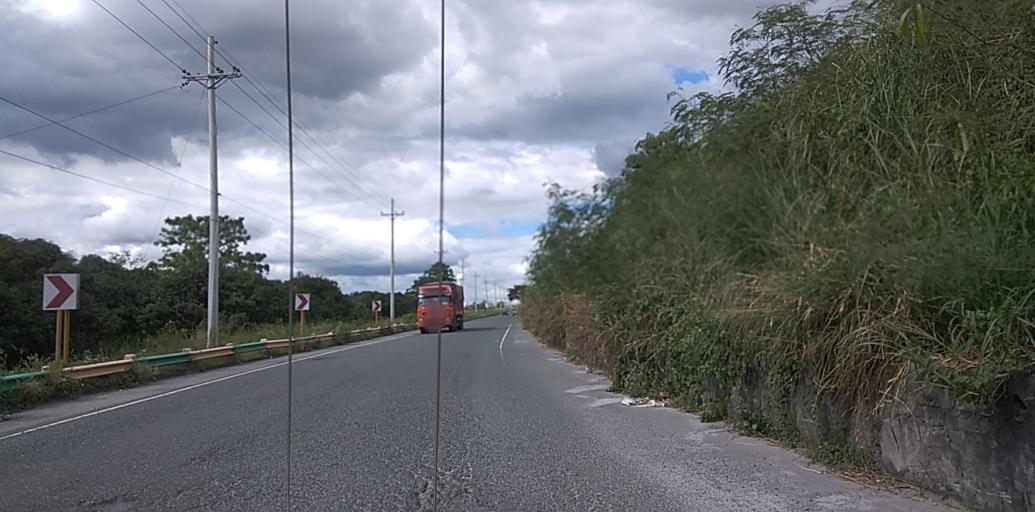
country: PH
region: Central Luzon
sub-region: Province of Pampanga
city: Dolores
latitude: 15.1058
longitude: 120.5208
